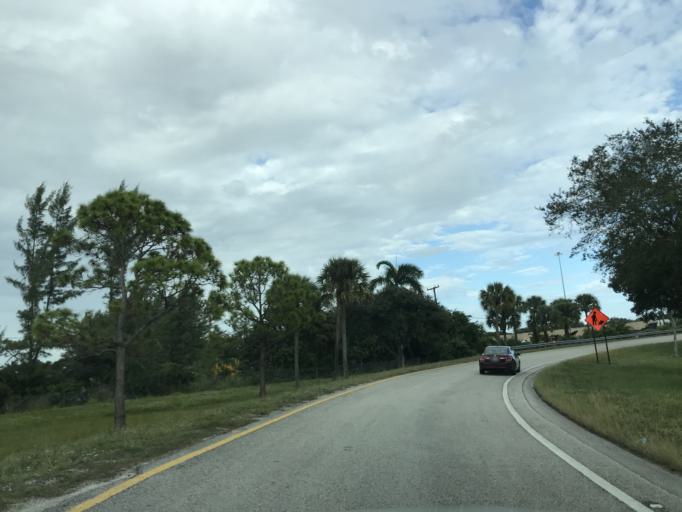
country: US
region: Florida
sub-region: Palm Beach County
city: Villages of Oriole
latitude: 26.5311
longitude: -80.1747
